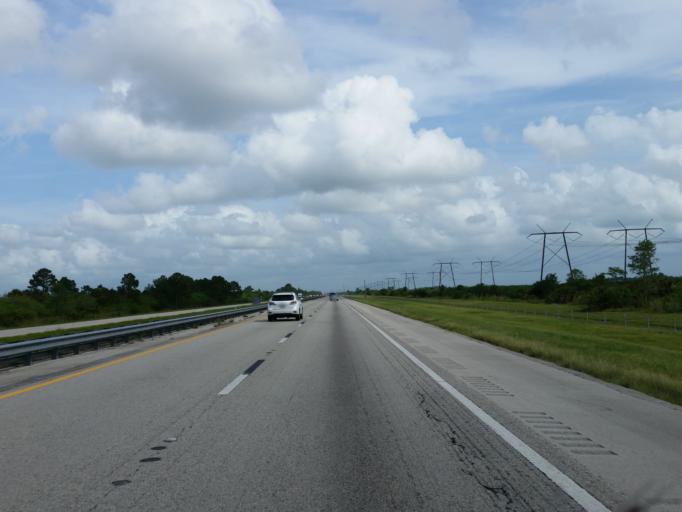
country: US
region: Florida
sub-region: Indian River County
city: West Vero Corridor
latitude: 27.5175
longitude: -80.5949
